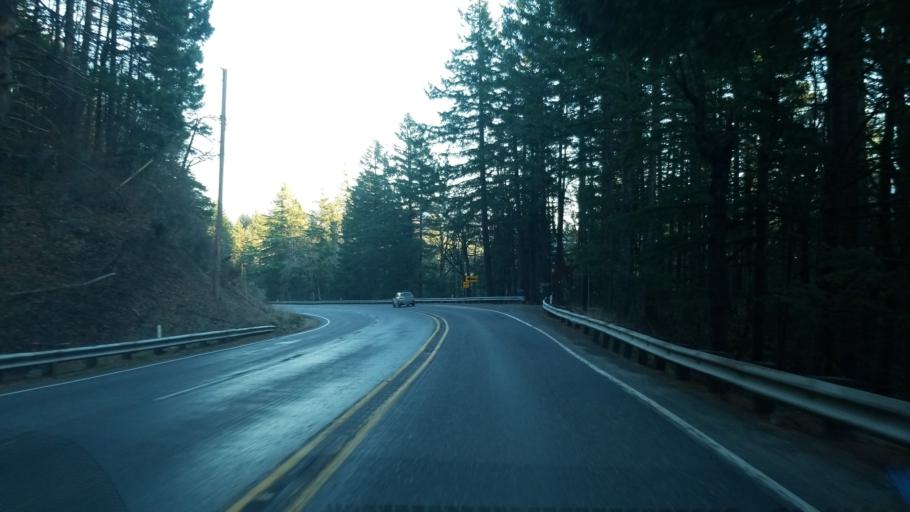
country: US
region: Washington
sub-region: Skamania County
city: Carson
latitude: 45.7155
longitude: -121.8249
